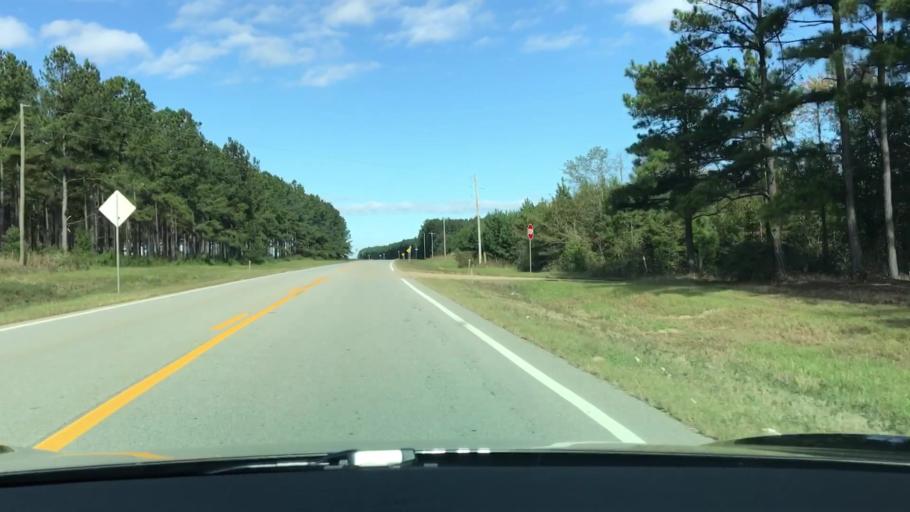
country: US
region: Georgia
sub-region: Glascock County
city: Gibson
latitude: 33.2793
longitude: -82.5034
